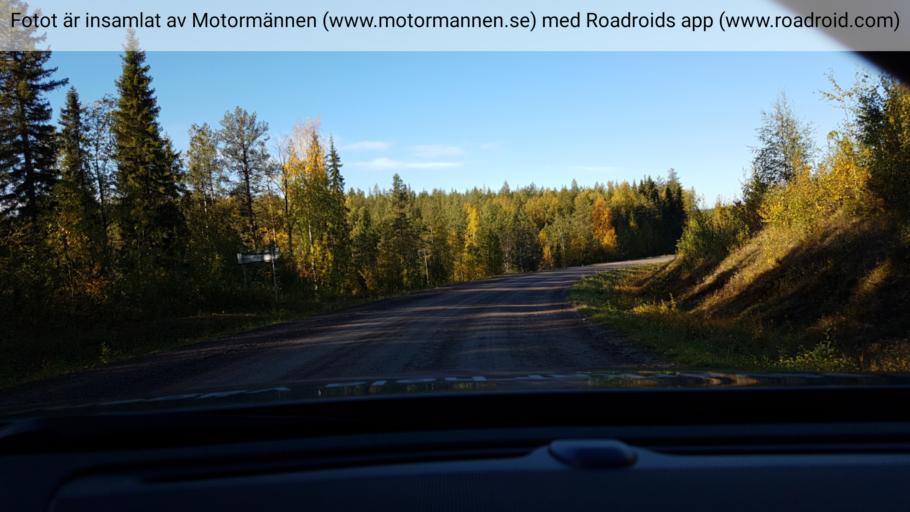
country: SE
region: Norrbotten
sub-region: Alvsbyns Kommun
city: AElvsbyn
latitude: 66.2581
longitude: 20.9587
